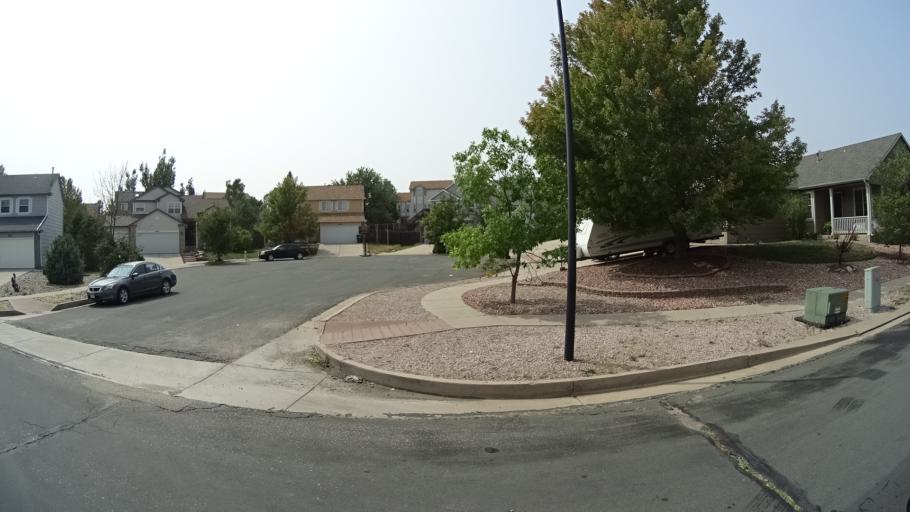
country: US
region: Colorado
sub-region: El Paso County
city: Cimarron Hills
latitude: 38.9202
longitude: -104.7357
